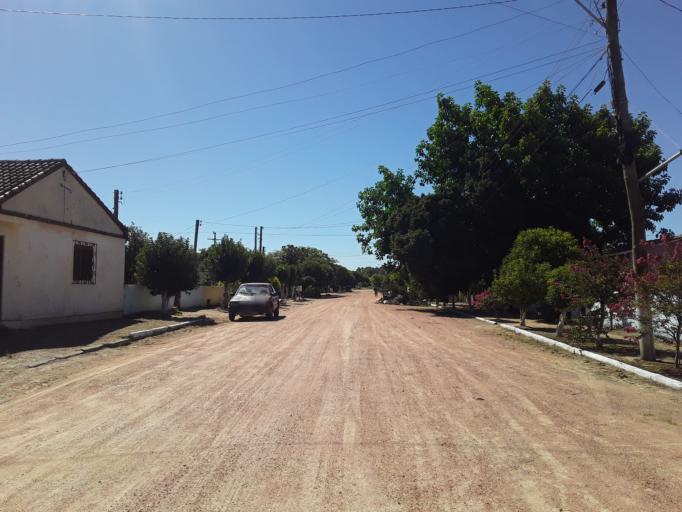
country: BR
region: Rio Grande do Sul
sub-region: Sao Lourenco Do Sul
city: Sao Lourenco do Sul
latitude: -31.3469
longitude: -51.9917
